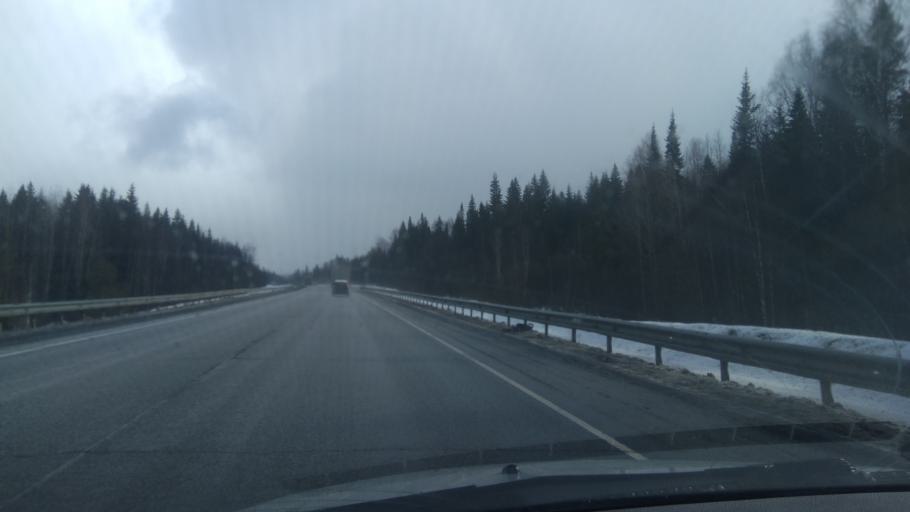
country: RU
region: Sverdlovsk
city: Arti
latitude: 56.7878
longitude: 58.5098
